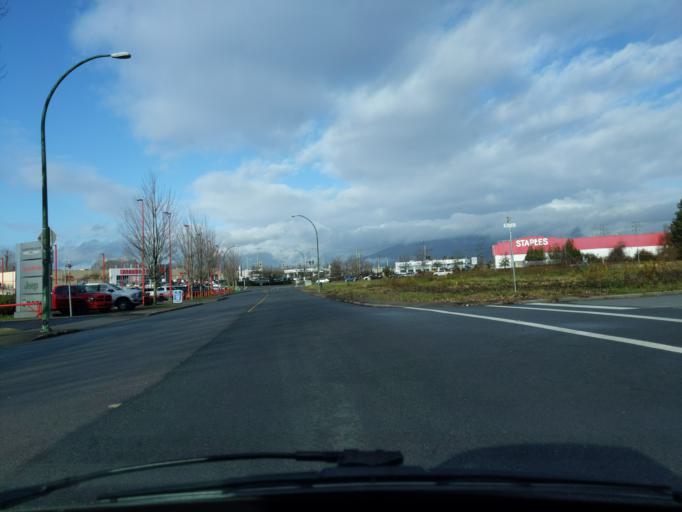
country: CA
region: British Columbia
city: Pitt Meadows
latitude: 49.2193
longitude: -122.6649
